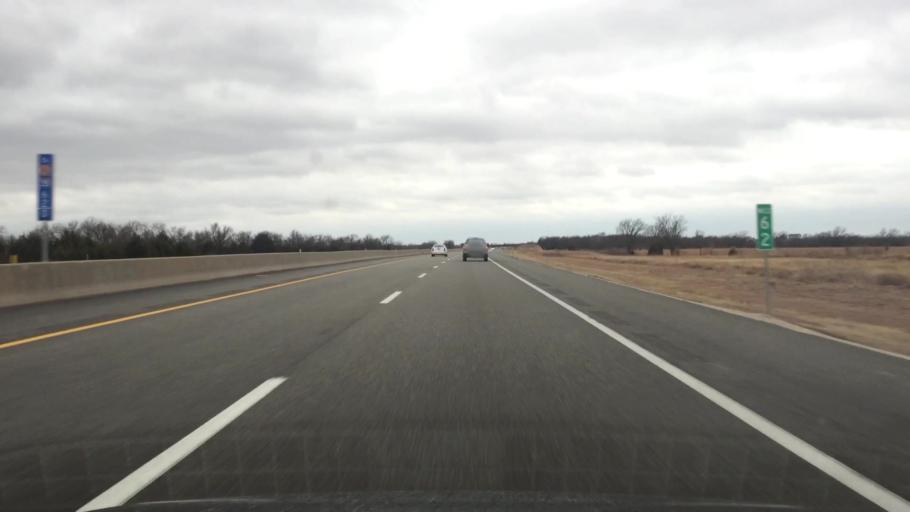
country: US
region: Kansas
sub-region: Butler County
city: Towanda
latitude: 37.7506
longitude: -97.0304
